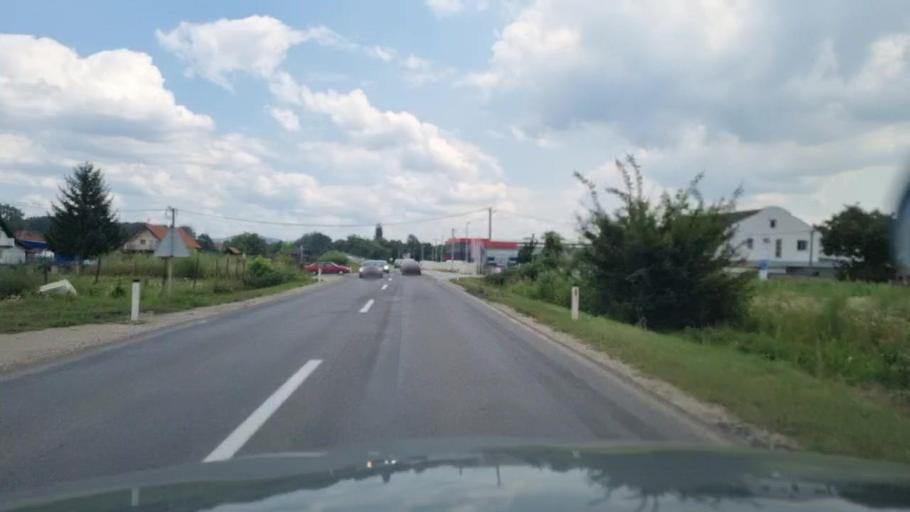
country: BA
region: Federation of Bosnia and Herzegovina
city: Kiseljak
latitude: 44.5130
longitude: 18.5573
